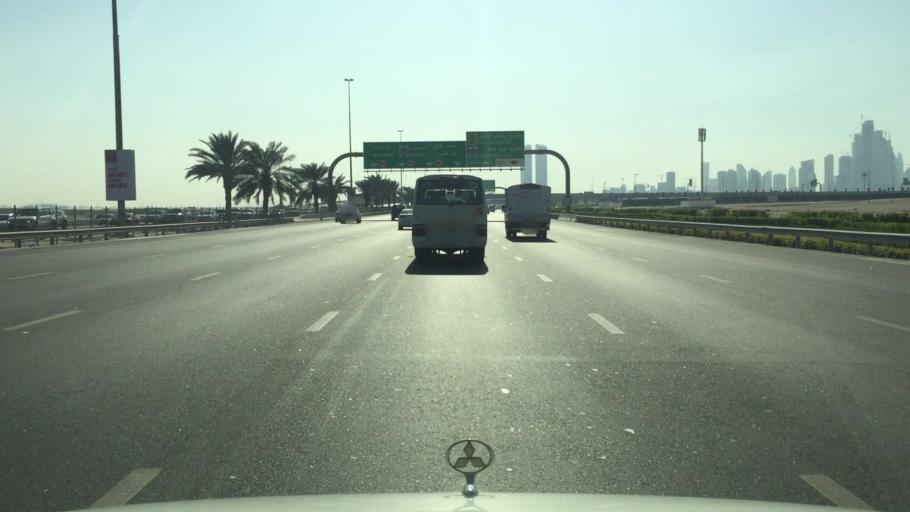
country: AE
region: Ash Shariqah
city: Sharjah
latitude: 25.2115
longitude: 55.3201
